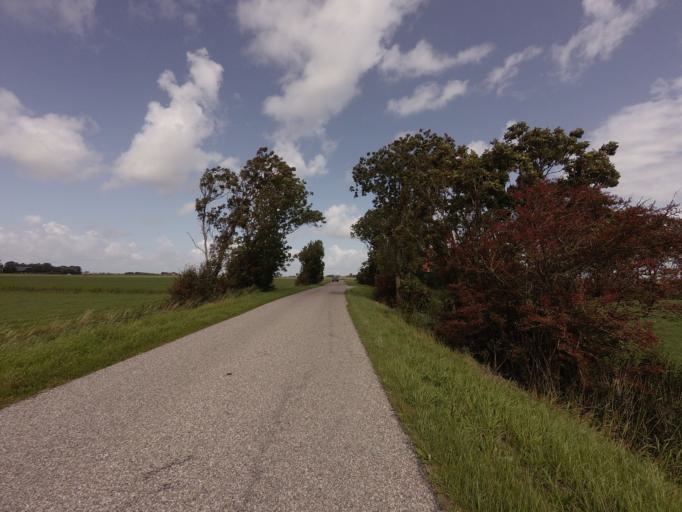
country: NL
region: Friesland
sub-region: Gemeente Franekeradeel
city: Sexbierum
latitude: 53.1603
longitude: 5.4834
